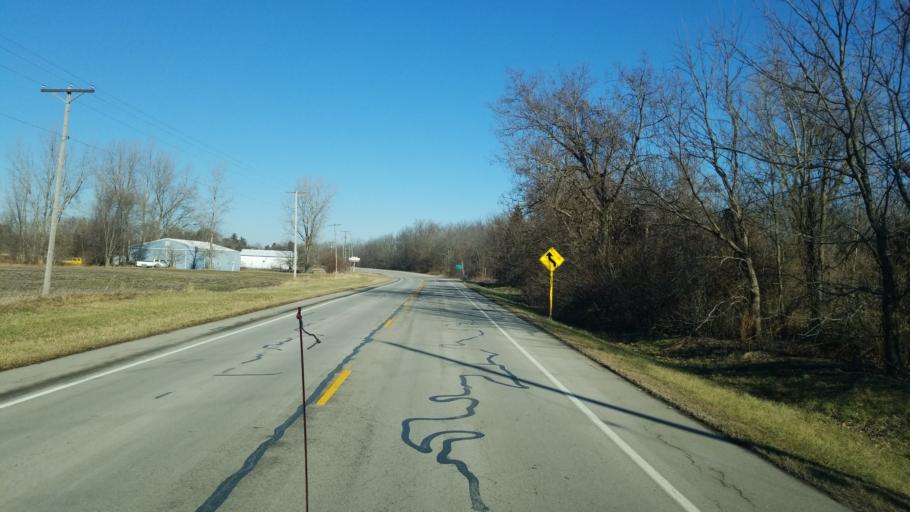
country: US
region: Ohio
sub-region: Lucas County
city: Whitehouse
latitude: 41.4557
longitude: -83.7851
